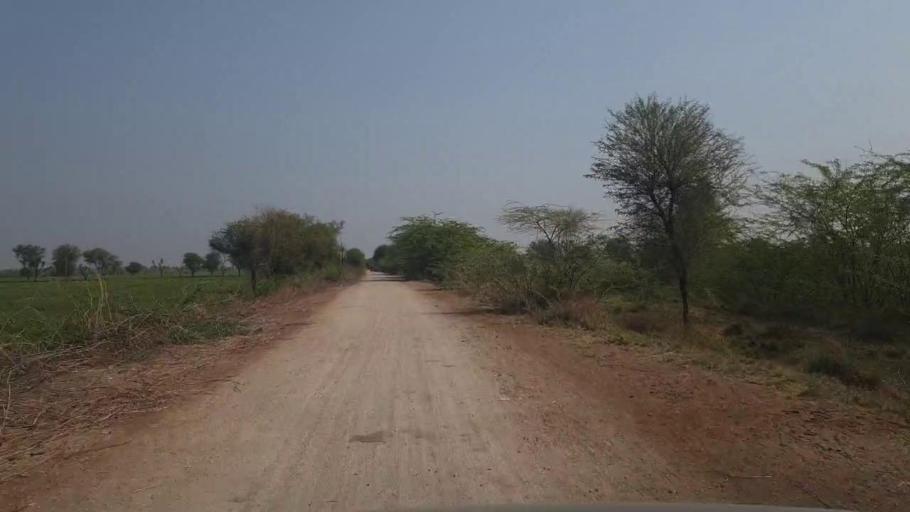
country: PK
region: Sindh
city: Umarkot
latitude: 25.4416
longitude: 69.6608
